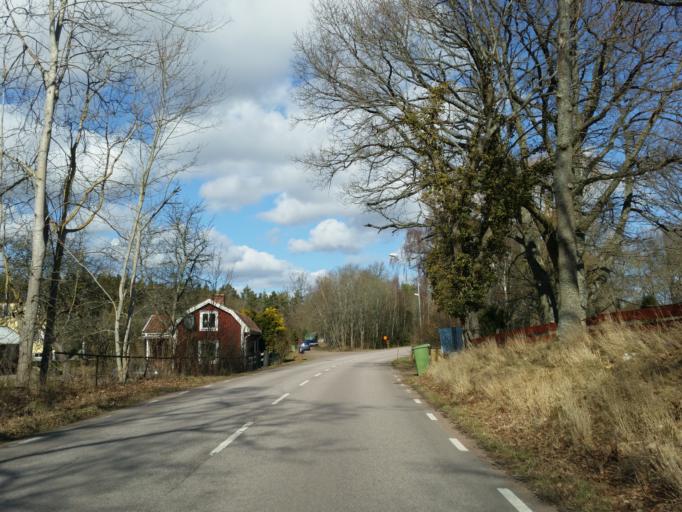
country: SE
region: Kalmar
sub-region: Monsteras Kommun
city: Timmernabben
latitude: 56.9082
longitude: 16.4327
